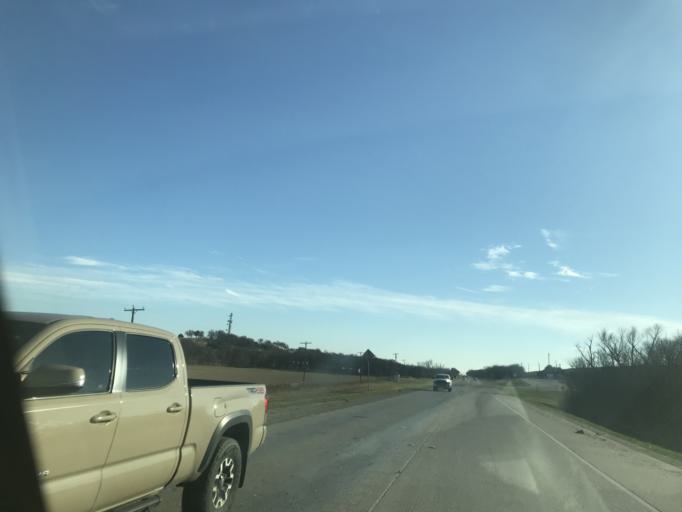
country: US
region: Texas
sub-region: Ellis County
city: Ferris
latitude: 32.5536
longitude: -96.6657
